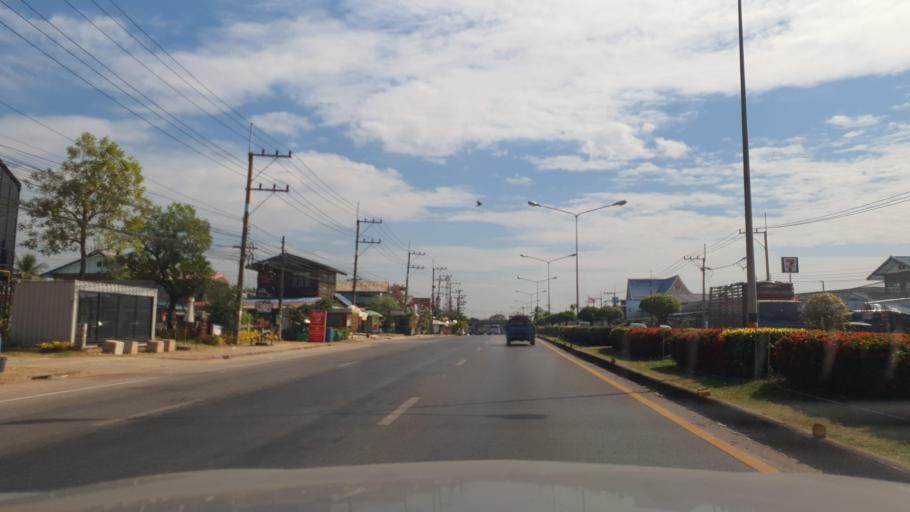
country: TH
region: Kalasin
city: Yang Talat
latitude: 16.4034
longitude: 103.4330
